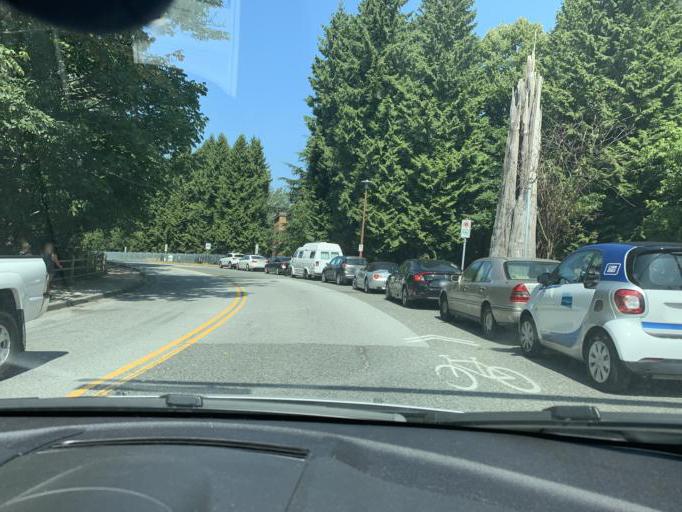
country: CA
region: British Columbia
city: West End
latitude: 49.2629
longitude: -123.2585
